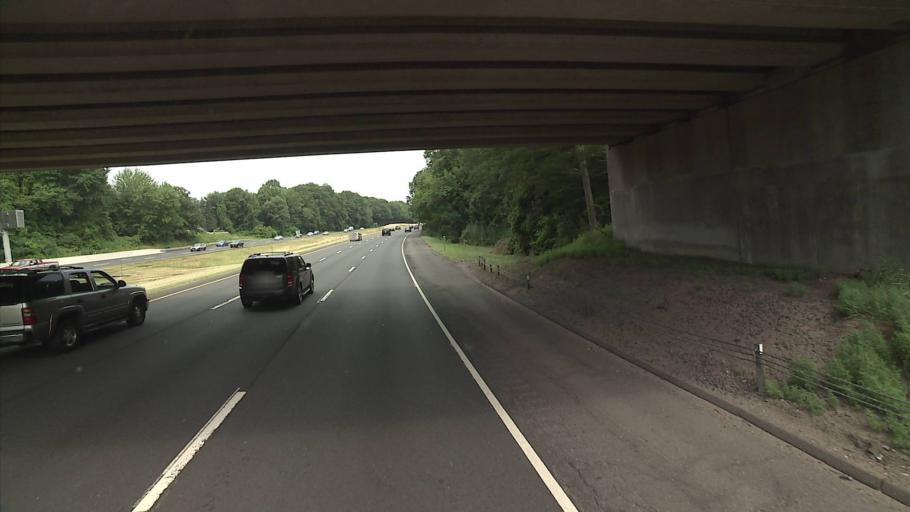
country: US
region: Connecticut
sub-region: New Haven County
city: Wolcott
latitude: 41.5918
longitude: -72.9026
